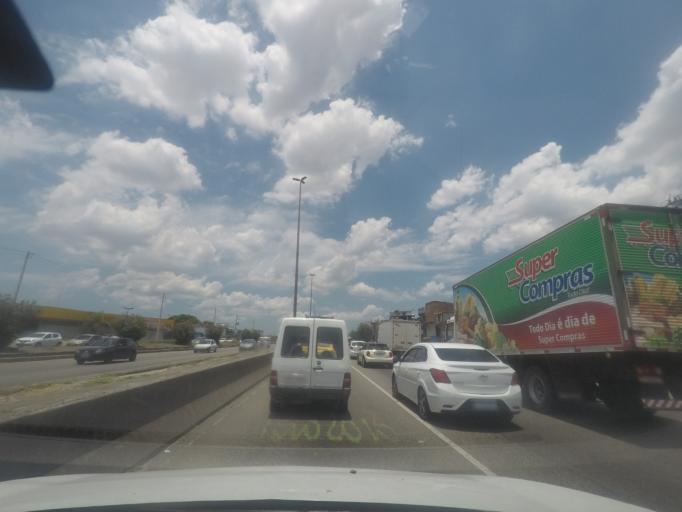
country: BR
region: Rio de Janeiro
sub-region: Sao Joao De Meriti
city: Sao Joao de Meriti
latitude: -22.8268
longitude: -43.3397
